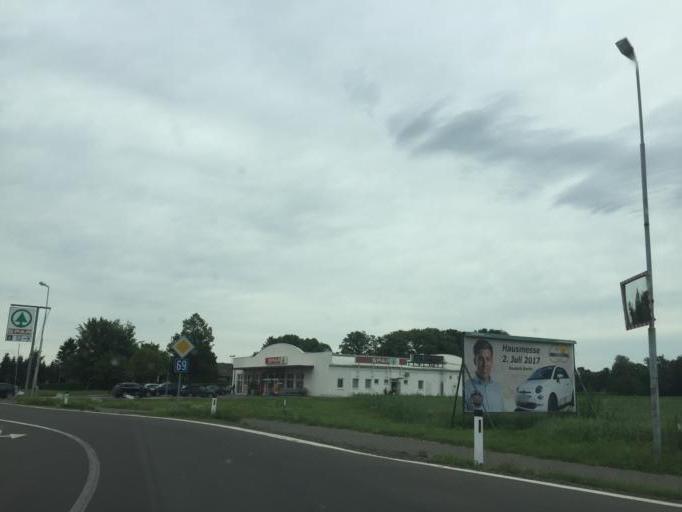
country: AT
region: Styria
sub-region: Politischer Bezirk Suedoststeiermark
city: Mureck
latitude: 46.7080
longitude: 15.7820
